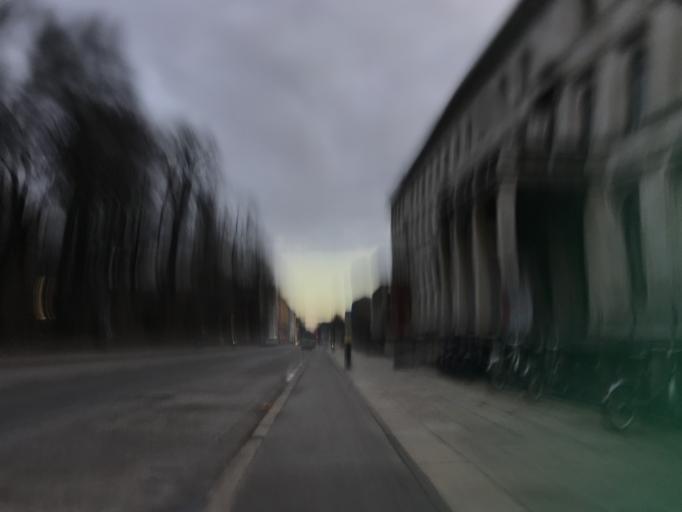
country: DE
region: Bavaria
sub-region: Upper Bavaria
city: Munich
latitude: 48.1457
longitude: 11.5669
